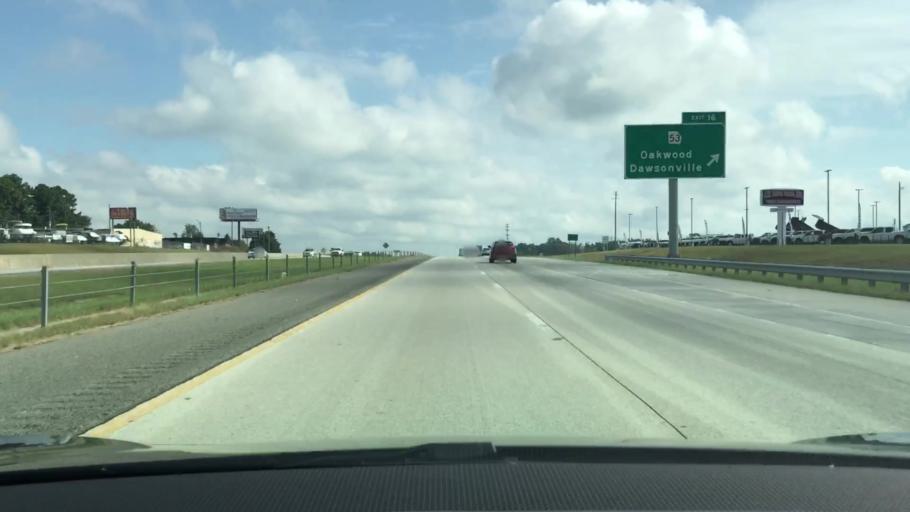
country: US
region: Georgia
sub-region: Hall County
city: Oakwood
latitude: 34.2216
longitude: -83.8728
